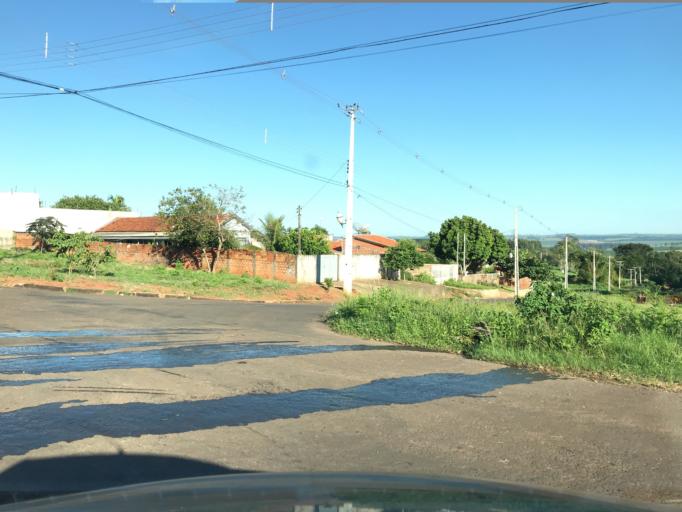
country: BR
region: Parana
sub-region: Ipora
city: Ipora
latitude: -23.9985
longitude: -53.7119
